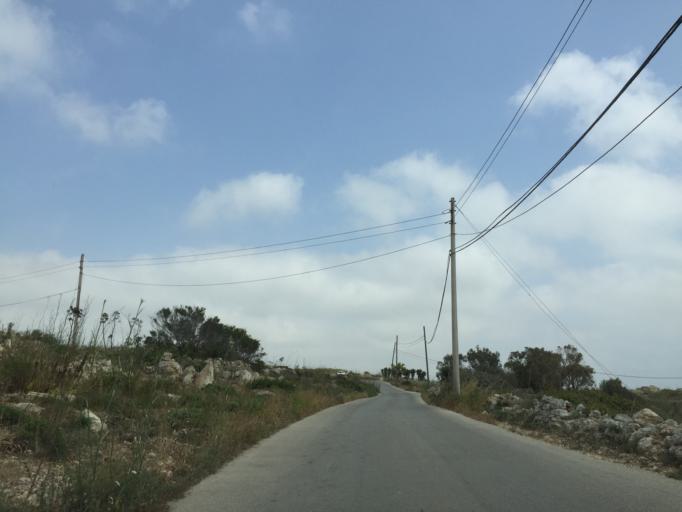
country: MT
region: L-Imgarr
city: Imgarr
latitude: 35.8988
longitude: 14.3538
